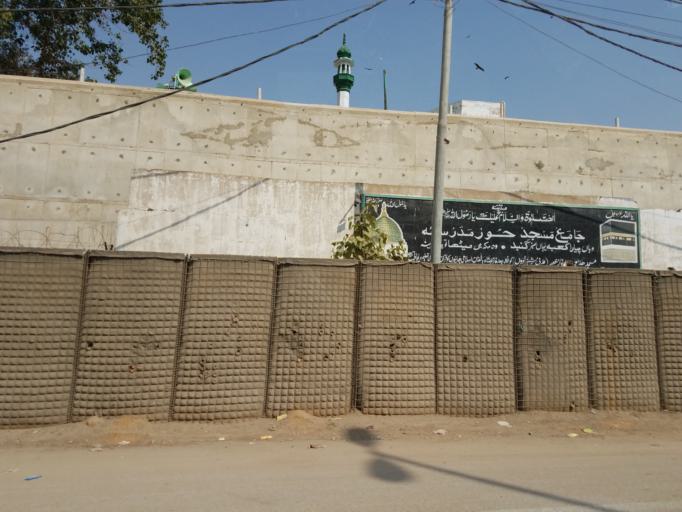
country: PK
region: Sindh
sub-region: Karachi District
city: Karachi
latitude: 24.8882
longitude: 67.0516
